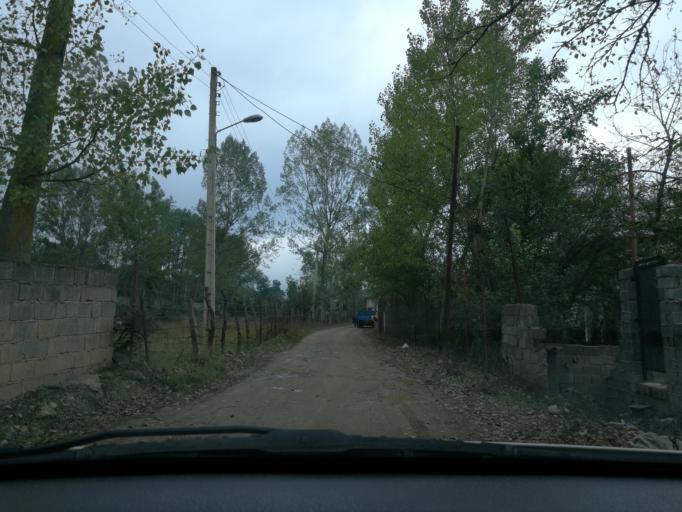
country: IR
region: Mazandaran
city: `Abbasabad
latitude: 36.5055
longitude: 51.1967
